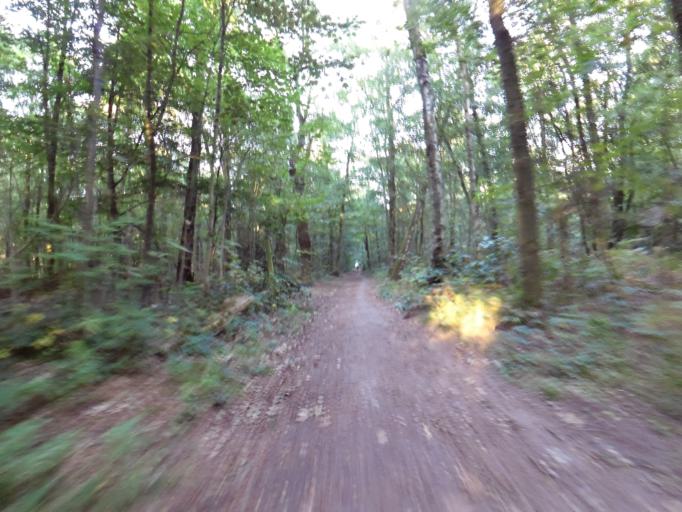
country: DE
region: North Rhine-Westphalia
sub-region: Regierungsbezirk Dusseldorf
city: Emmerich
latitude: 51.8670
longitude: 6.1862
